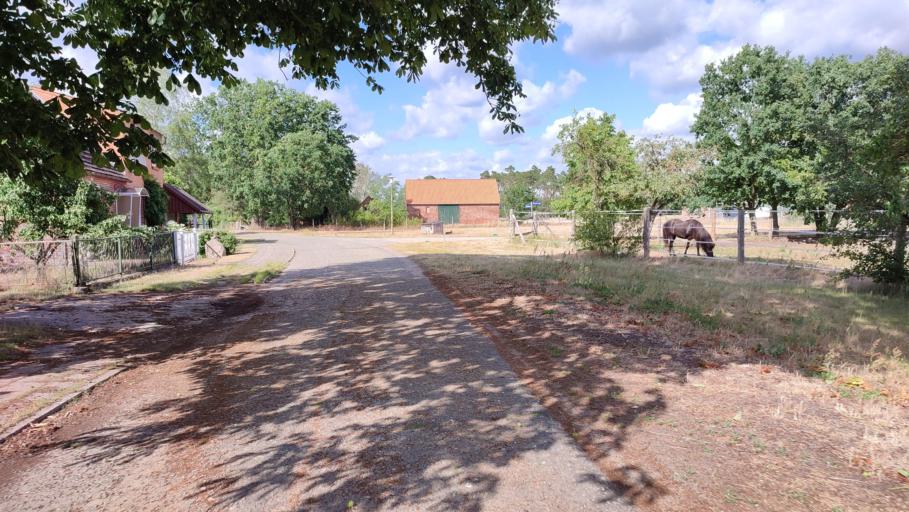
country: DE
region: Lower Saxony
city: Damnatz
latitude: 53.1730
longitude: 11.1686
